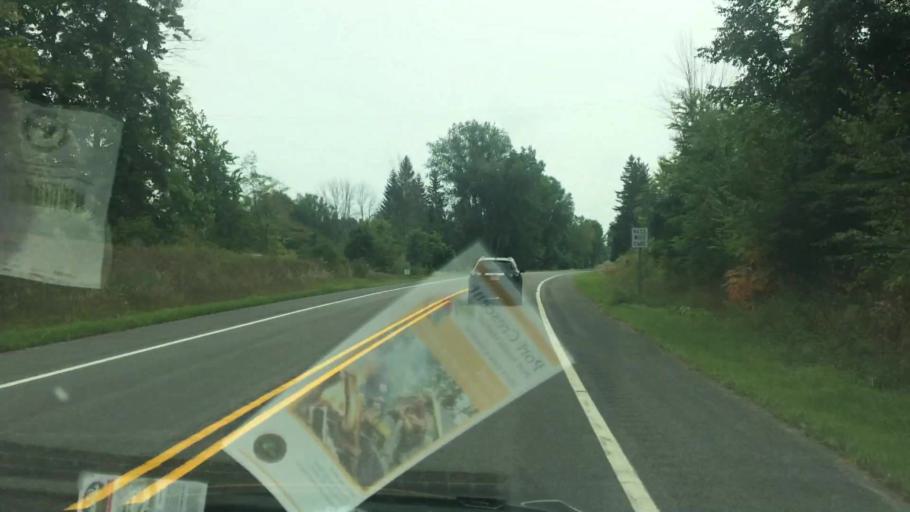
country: US
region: Michigan
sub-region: Huron County
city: Harbor Beach
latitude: 44.0197
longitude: -82.8069
